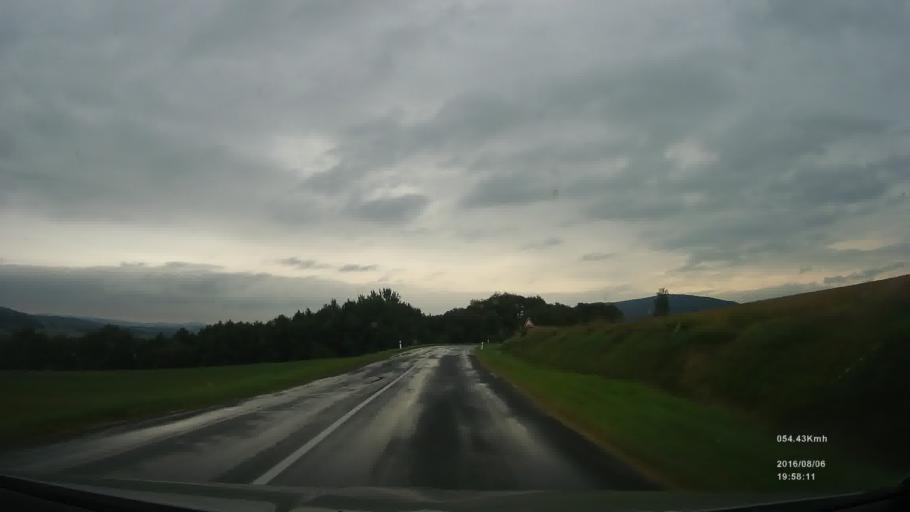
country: SK
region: Presovsky
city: Svidnik
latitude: 49.2709
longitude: 21.5798
